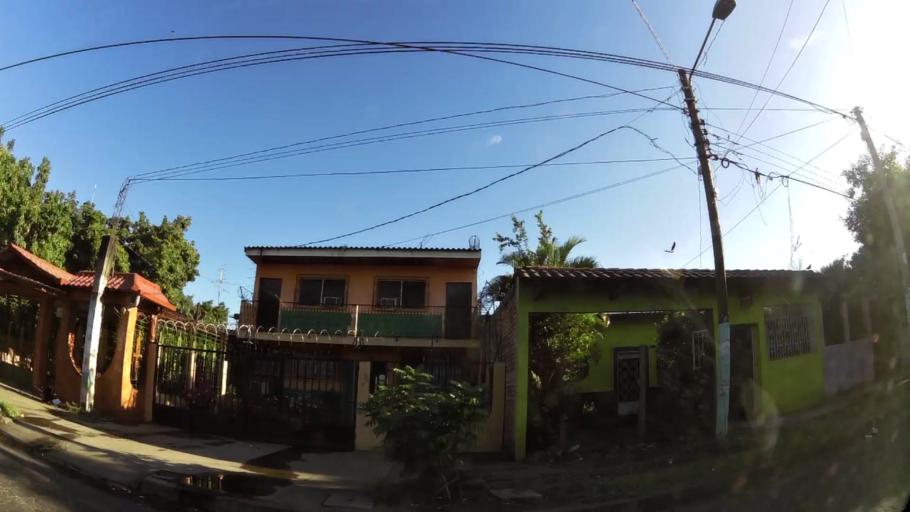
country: SV
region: Sonsonate
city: Sonsonate
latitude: 13.7178
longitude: -89.7301
